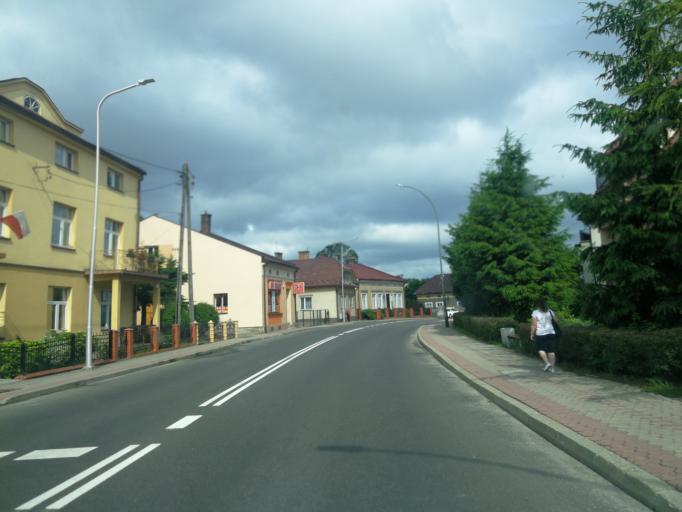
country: PL
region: Subcarpathian Voivodeship
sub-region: Powiat leski
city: Lesko
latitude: 49.4667
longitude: 22.3332
